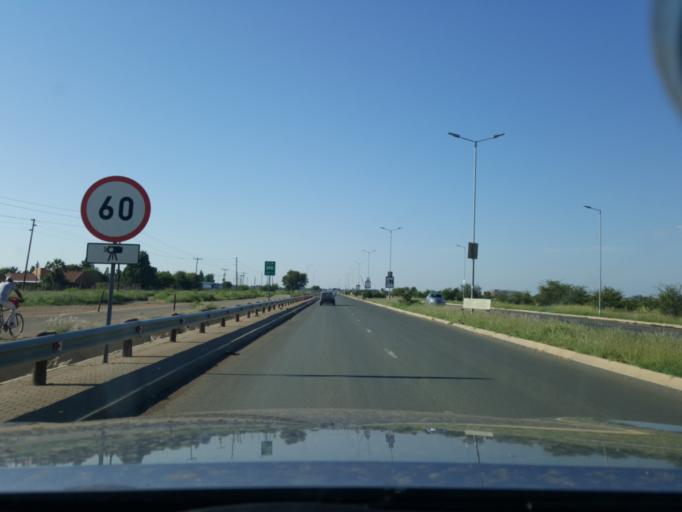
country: ZA
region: North-West
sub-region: Ngaka Modiri Molema District Municipality
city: Mmabatho
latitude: -25.8217
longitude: 25.6350
